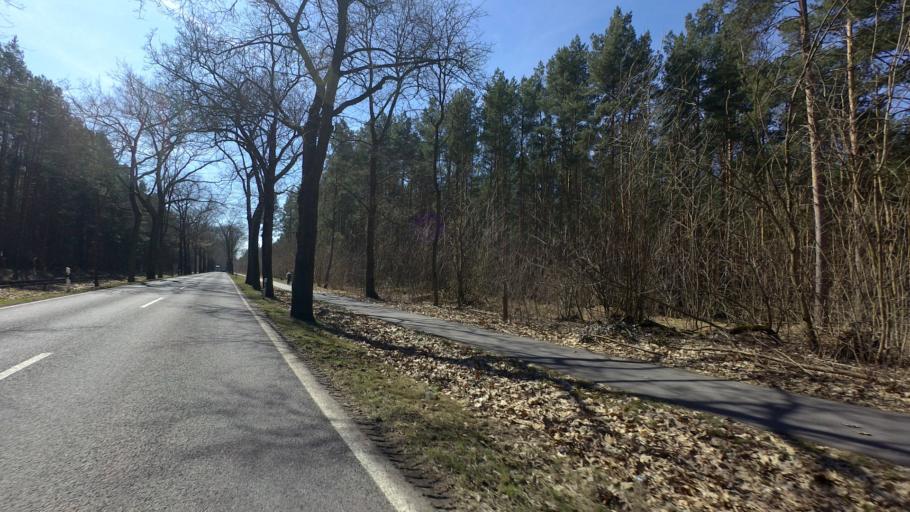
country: DE
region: Brandenburg
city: Schwerin
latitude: 52.1901
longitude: 13.5811
